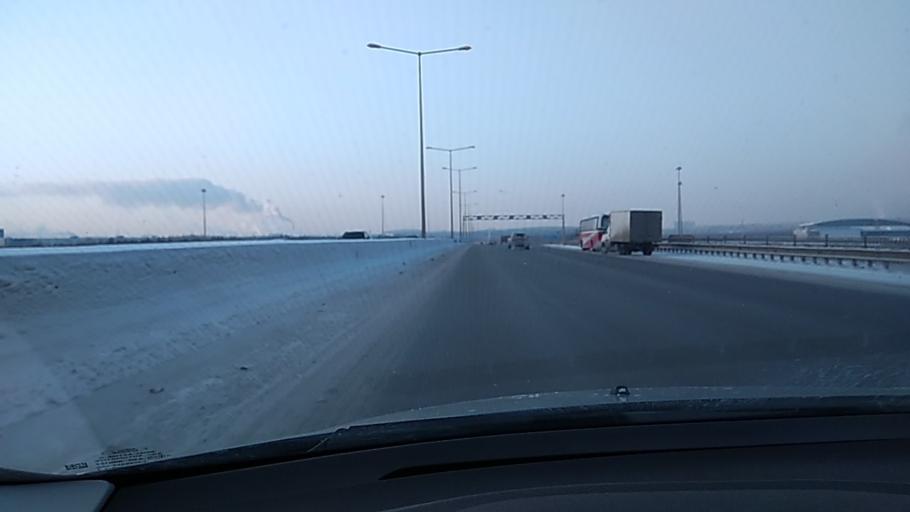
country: RU
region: Sverdlovsk
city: Istok
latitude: 56.7615
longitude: 60.7708
